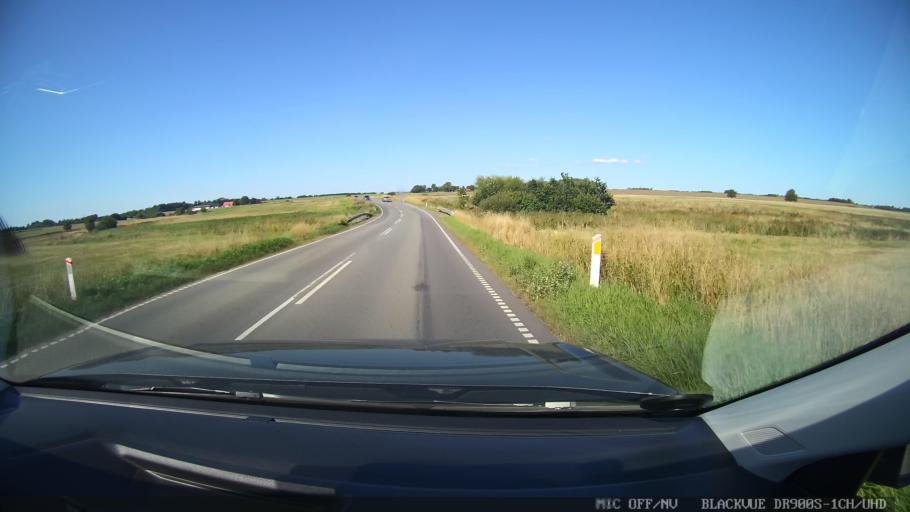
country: DK
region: Central Jutland
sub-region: Randers Kommune
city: Spentrup
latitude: 56.5352
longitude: 9.9994
